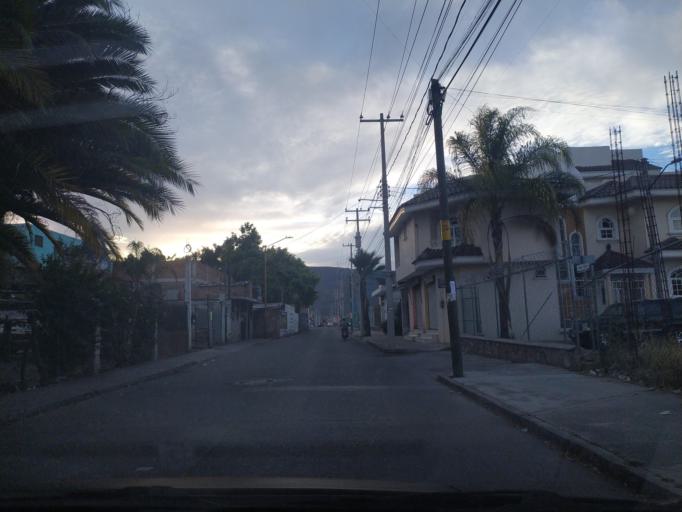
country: LA
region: Oudomxai
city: Muang La
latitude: 21.0170
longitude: 101.8677
